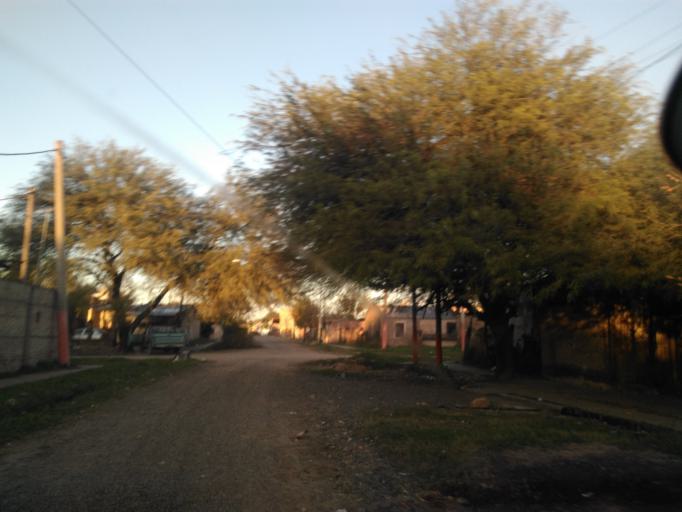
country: AR
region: Chaco
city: Resistencia
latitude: -27.4778
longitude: -58.9899
